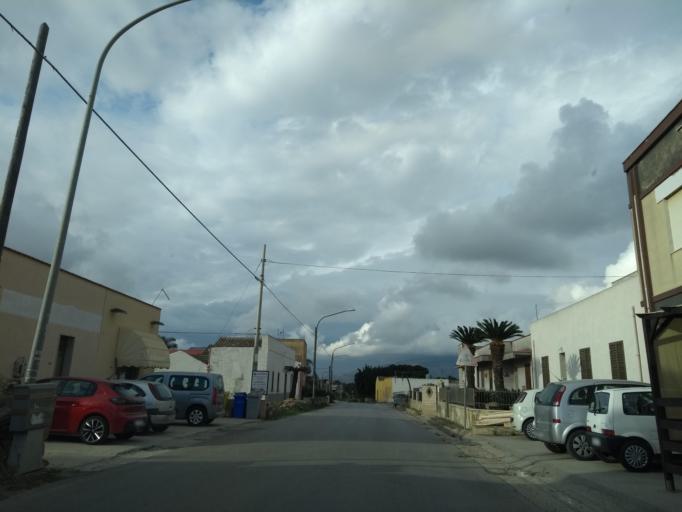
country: IT
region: Sicily
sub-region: Trapani
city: Marausa
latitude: 37.9527
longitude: 12.5152
